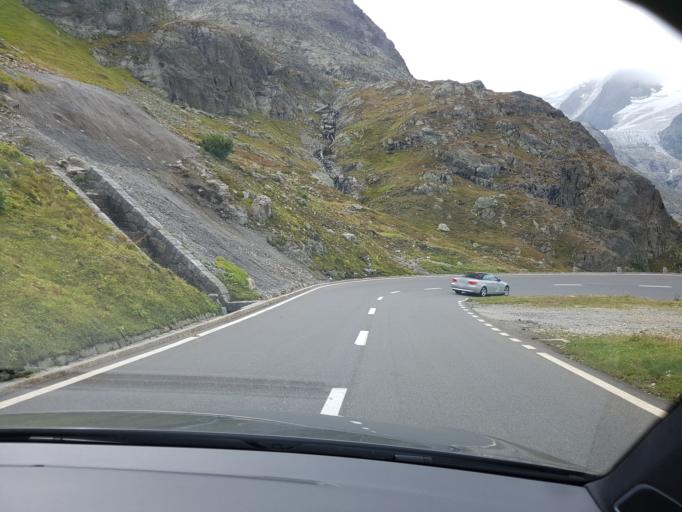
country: CH
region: Obwalden
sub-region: Obwalden
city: Engelberg
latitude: 46.7270
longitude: 8.4419
